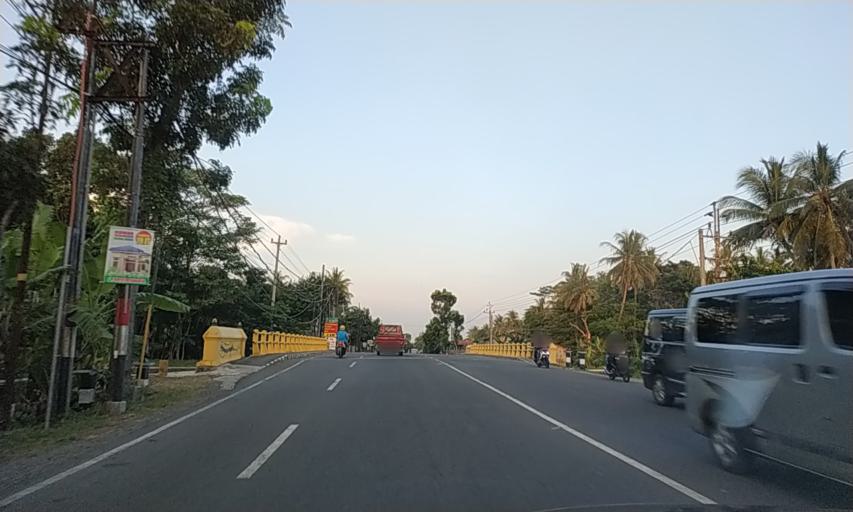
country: ID
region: Daerah Istimewa Yogyakarta
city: Srandakan
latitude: -7.8901
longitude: 110.1058
